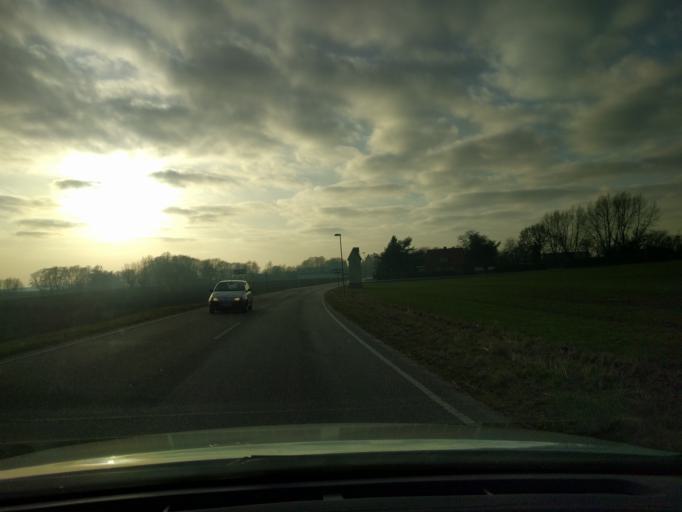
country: DK
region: Zealand
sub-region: Guldborgsund Kommune
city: Nykobing Falster
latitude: 54.7713
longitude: 11.9855
